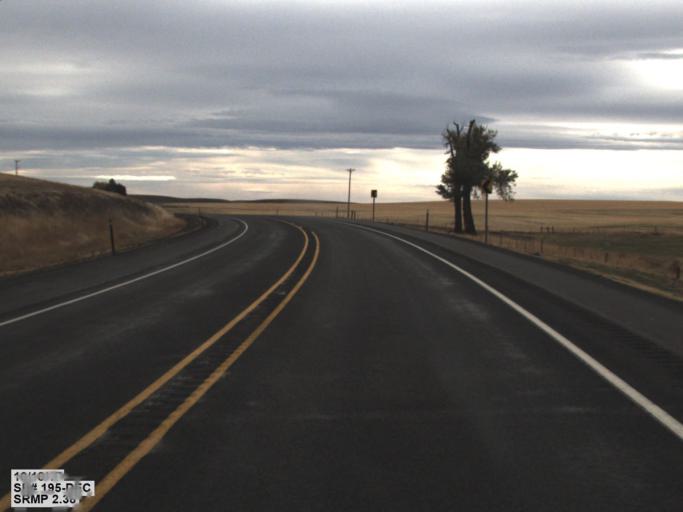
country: US
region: Washington
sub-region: Asotin County
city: Clarkston
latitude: 46.4989
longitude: -117.0779
